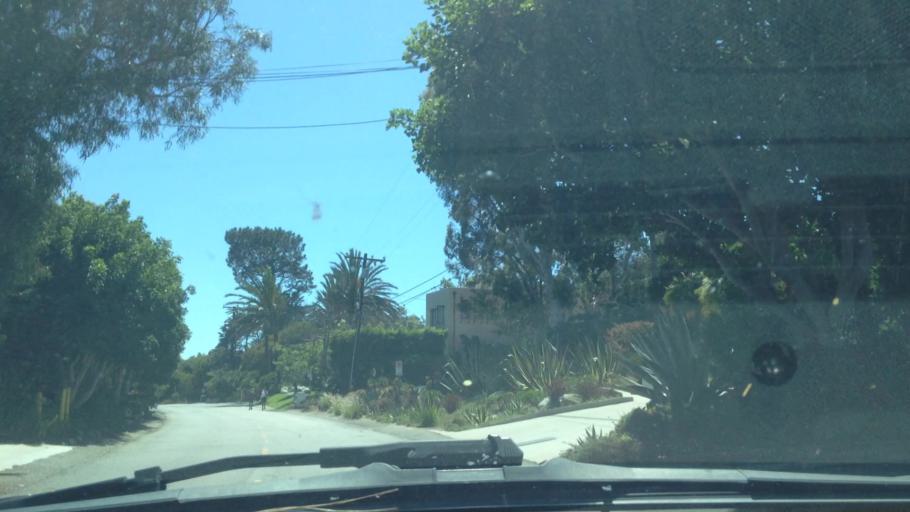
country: US
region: California
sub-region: Los Angeles County
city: Malibu
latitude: 34.0064
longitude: -118.8035
